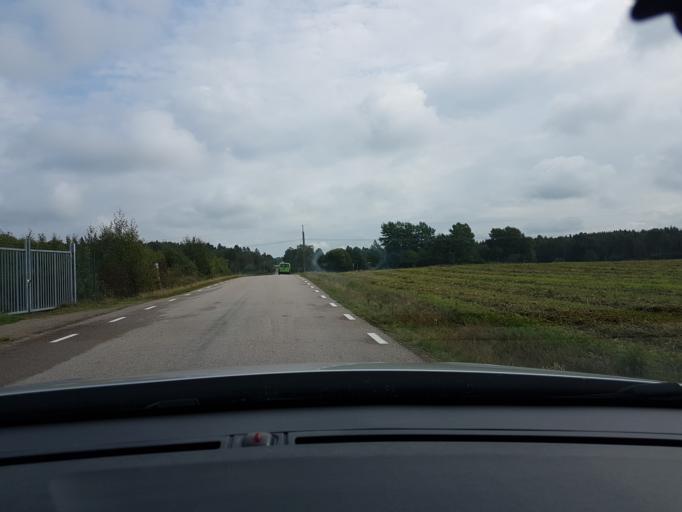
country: SE
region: Vaestra Goetaland
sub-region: Ale Kommun
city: Alvangen
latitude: 57.9132
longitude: 12.1460
